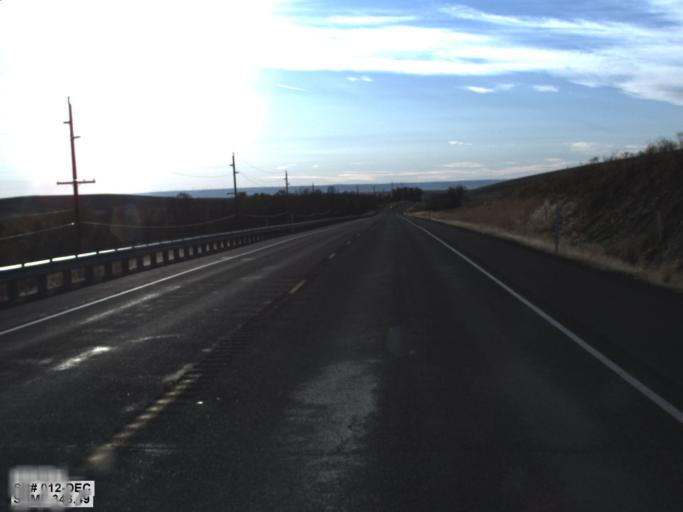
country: US
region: Washington
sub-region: Walla Walla County
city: Waitsburg
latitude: 46.1319
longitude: -118.1803
